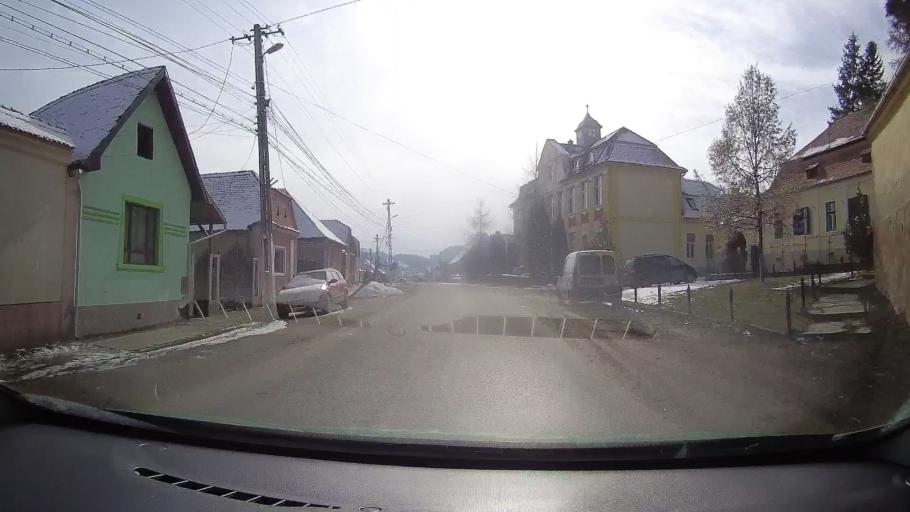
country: RO
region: Sibiu
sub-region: Comuna Laslea
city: Laslea
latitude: 46.2101
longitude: 24.6570
